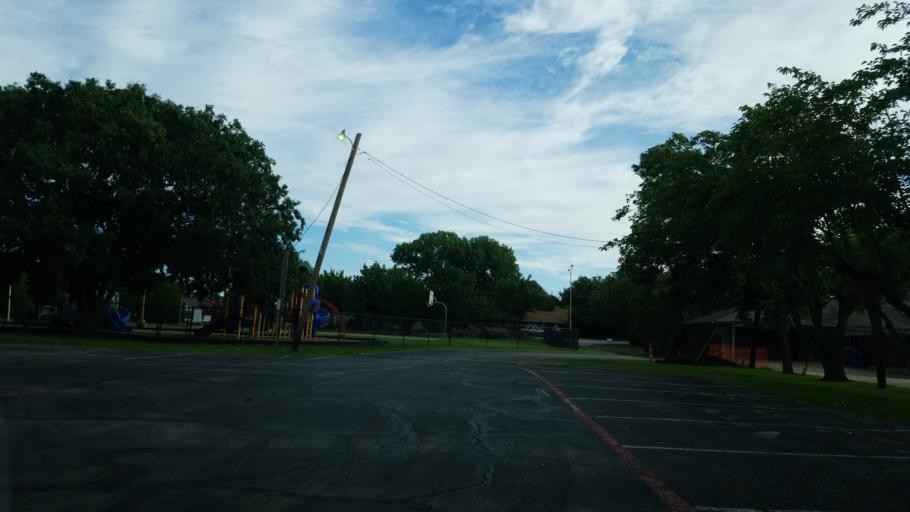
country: US
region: Texas
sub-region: Dallas County
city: Farmers Branch
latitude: 32.8942
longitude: -96.8548
